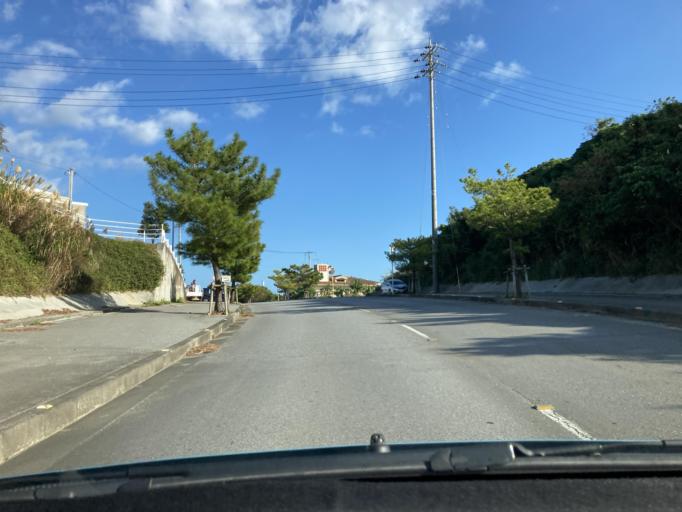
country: JP
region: Okinawa
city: Gushikawa
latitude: 26.3840
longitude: 127.8485
